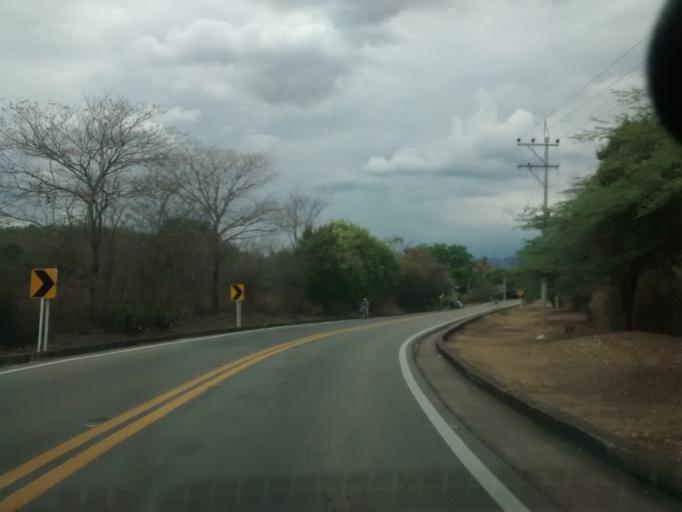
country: CO
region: Cundinamarca
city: Tocaima
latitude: 4.4340
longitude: -74.6869
